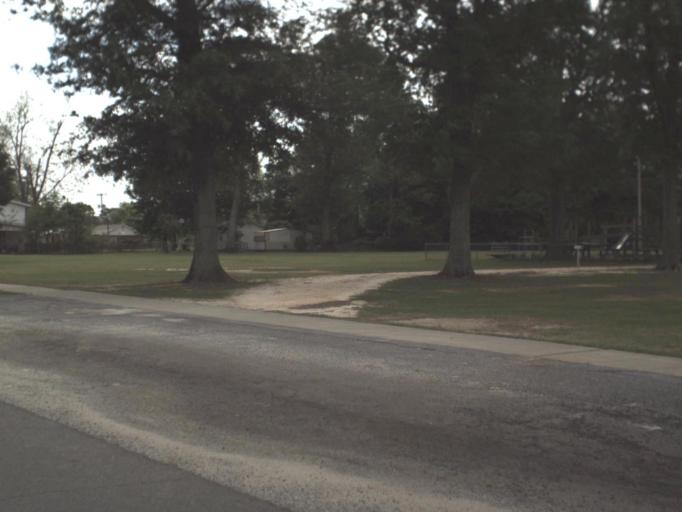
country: US
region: Florida
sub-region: Escambia County
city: Century
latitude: 30.9491
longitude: -87.1521
